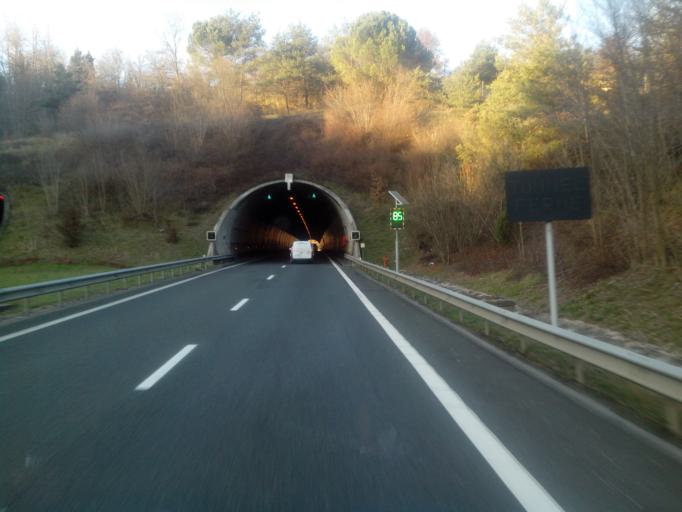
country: FR
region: Limousin
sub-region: Departement de la Correze
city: Brive-la-Gaillarde
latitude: 45.1010
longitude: 1.5191
